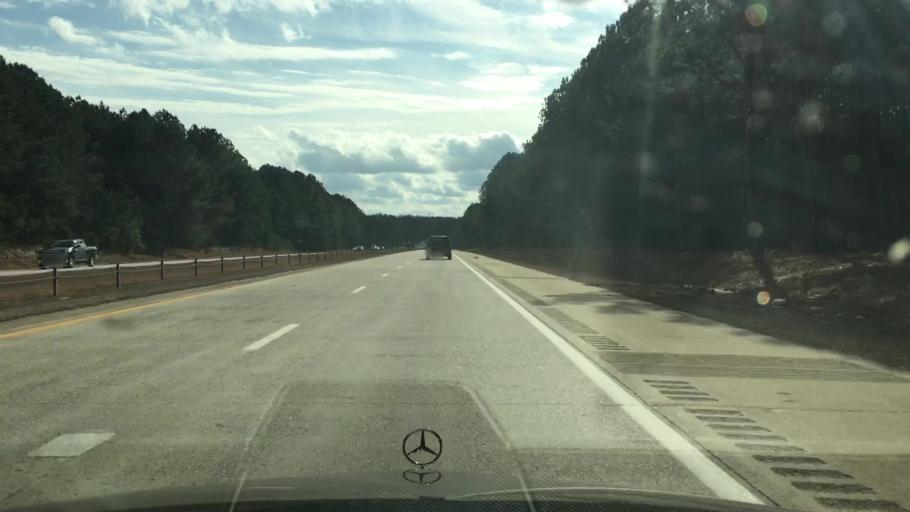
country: US
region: North Carolina
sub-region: Johnston County
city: Clayton
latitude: 35.5715
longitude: -78.5764
